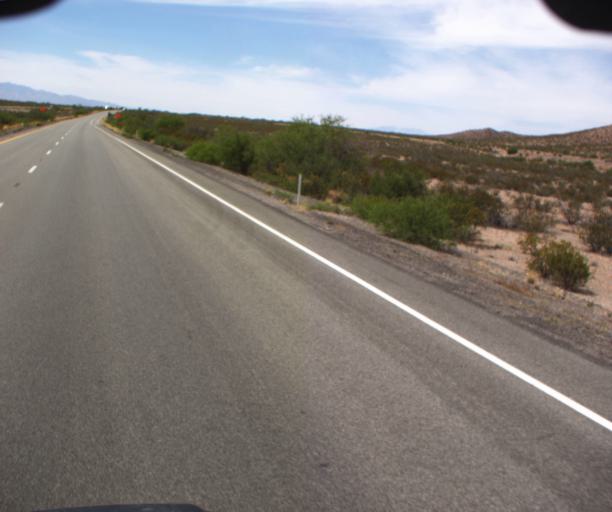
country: US
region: New Mexico
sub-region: Hidalgo County
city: Lordsburg
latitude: 32.2392
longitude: -109.0938
